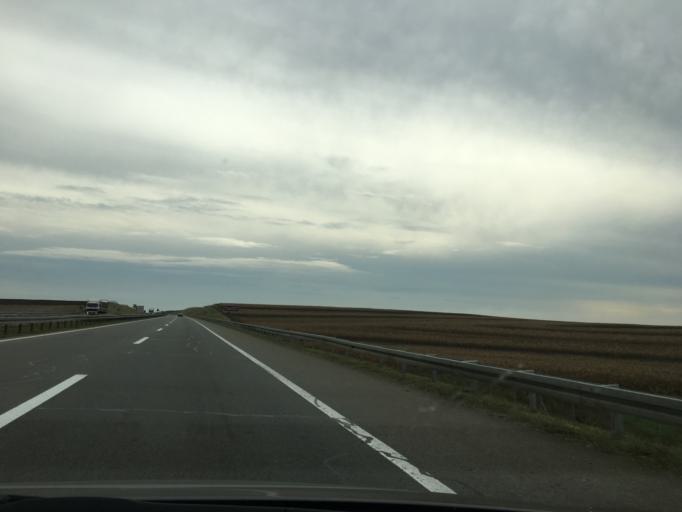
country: RS
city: Beska
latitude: 45.1287
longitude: 20.0909
